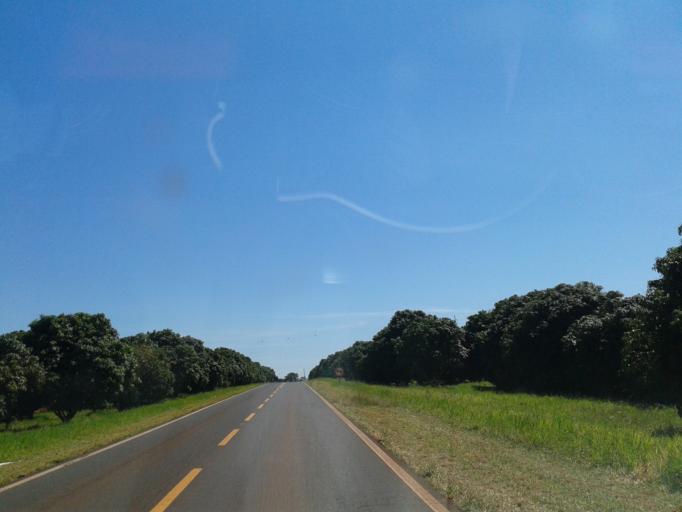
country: BR
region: Minas Gerais
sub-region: Centralina
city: Centralina
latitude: -18.7159
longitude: -49.1389
